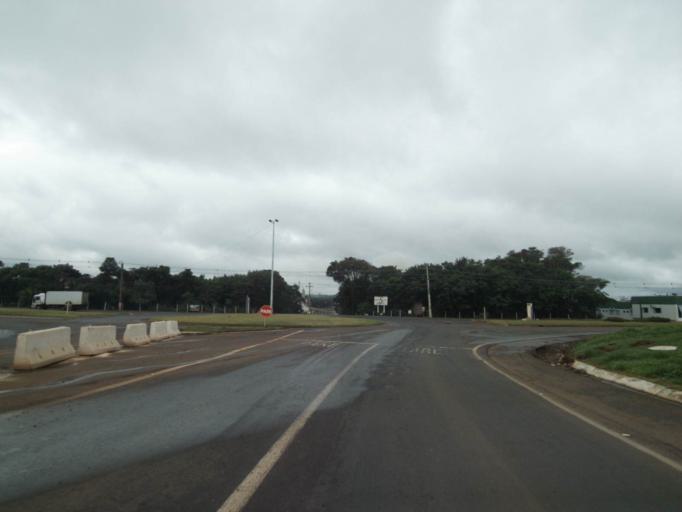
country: BR
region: Parana
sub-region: Marechal Candido Rondon
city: Marechal Candido Rondon
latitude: -24.5679
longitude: -54.0342
